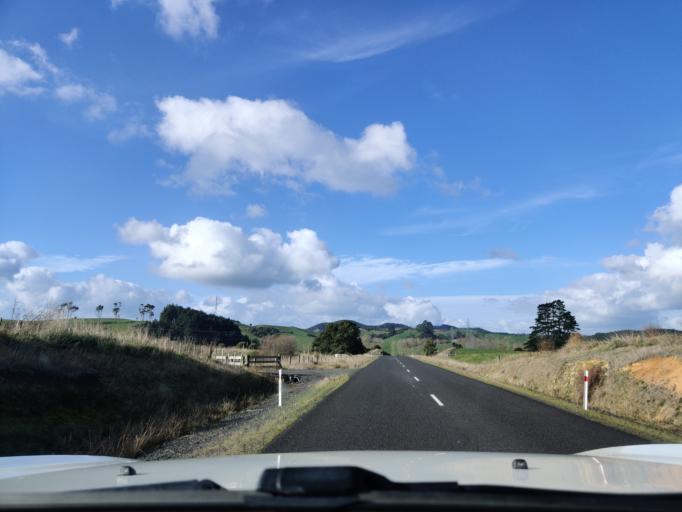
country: NZ
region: Waikato
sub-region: Waikato District
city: Te Kauwhata
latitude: -37.2831
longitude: 175.2035
